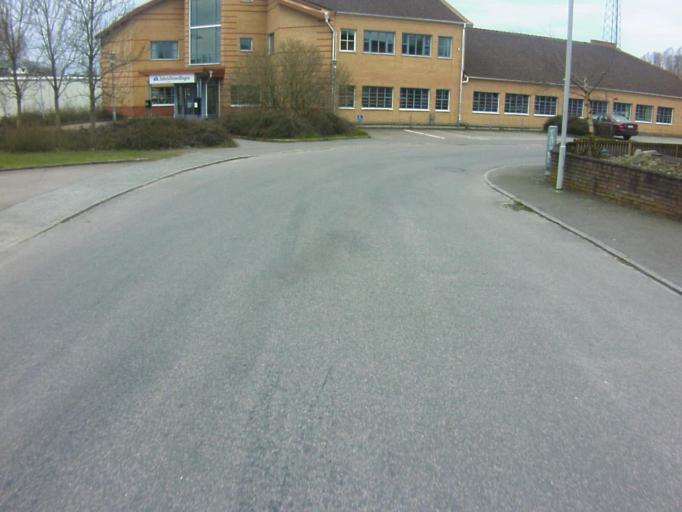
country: SE
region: Skane
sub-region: Kavlinge Kommun
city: Kaevlinge
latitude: 55.7899
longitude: 13.1034
